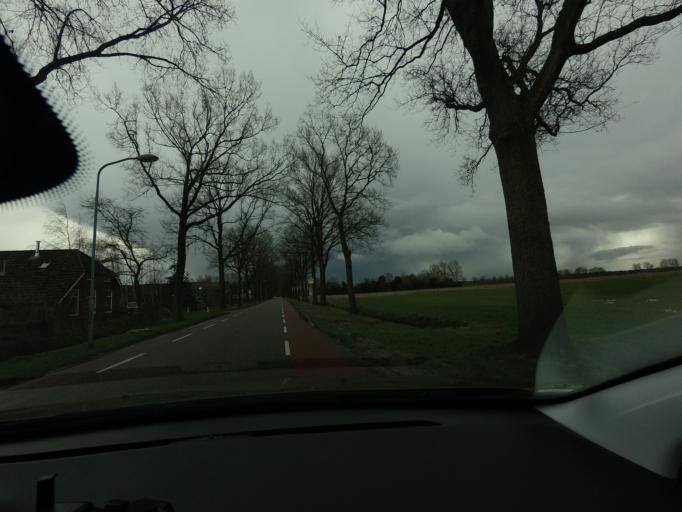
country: NL
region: Drenthe
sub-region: Gemeente Borger-Odoorn
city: Borger
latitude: 52.9834
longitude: 6.7837
